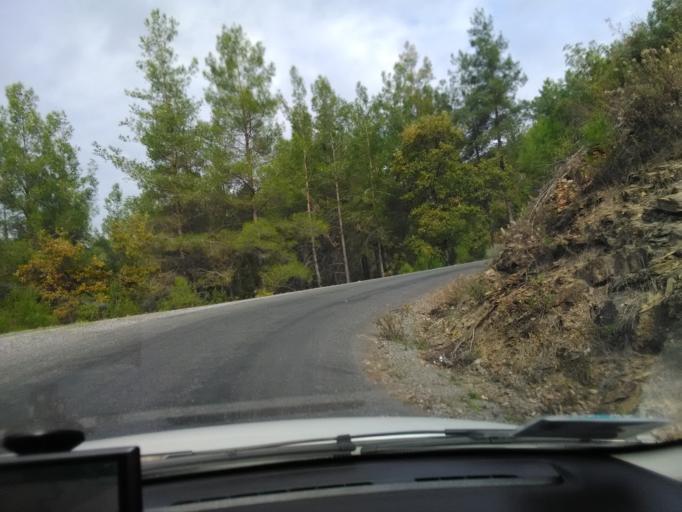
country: TR
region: Antalya
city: Gazipasa
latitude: 36.2441
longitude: 32.4199
